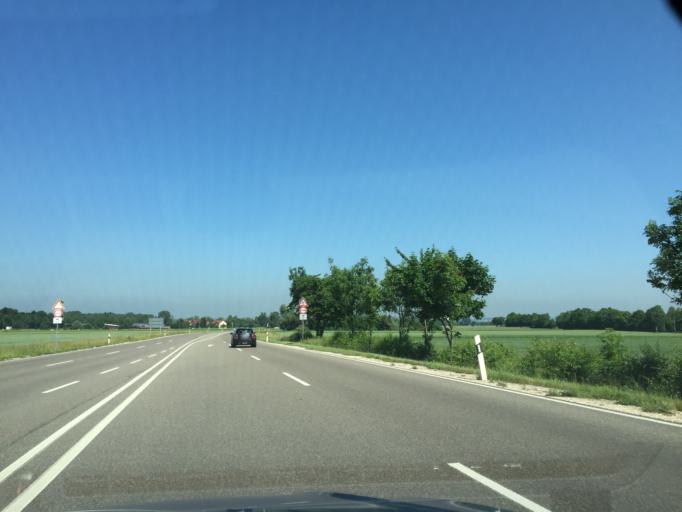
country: DE
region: Bavaria
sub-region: Swabia
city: Senden
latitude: 48.3411
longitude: 10.0308
